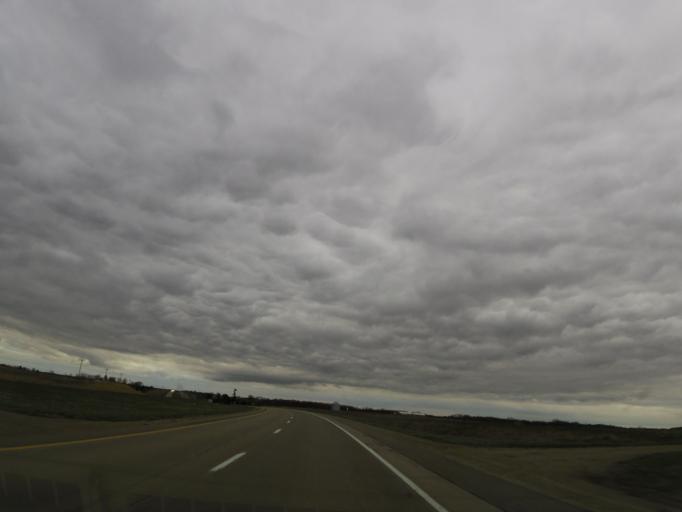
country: US
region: Iowa
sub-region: Henry County
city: Mount Pleasant
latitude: 41.0361
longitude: -91.5485
